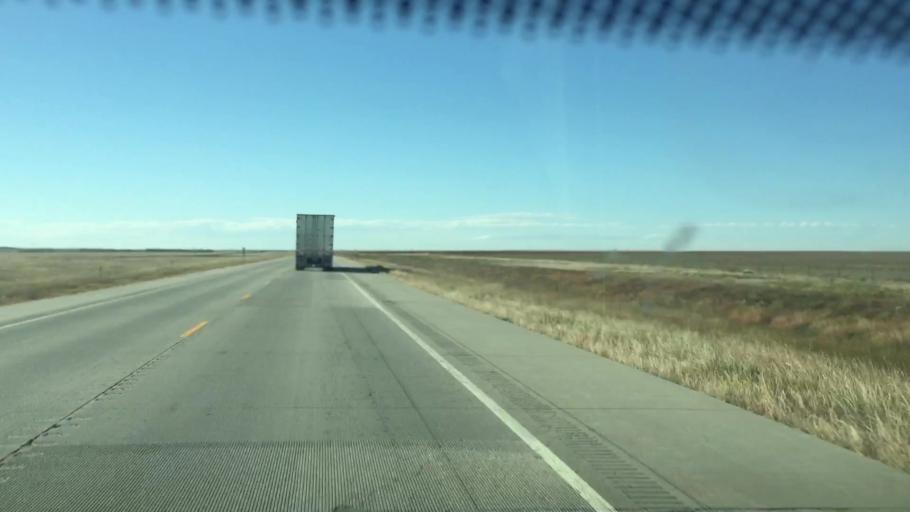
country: US
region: Colorado
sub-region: Kiowa County
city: Eads
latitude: 38.7927
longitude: -102.9390
